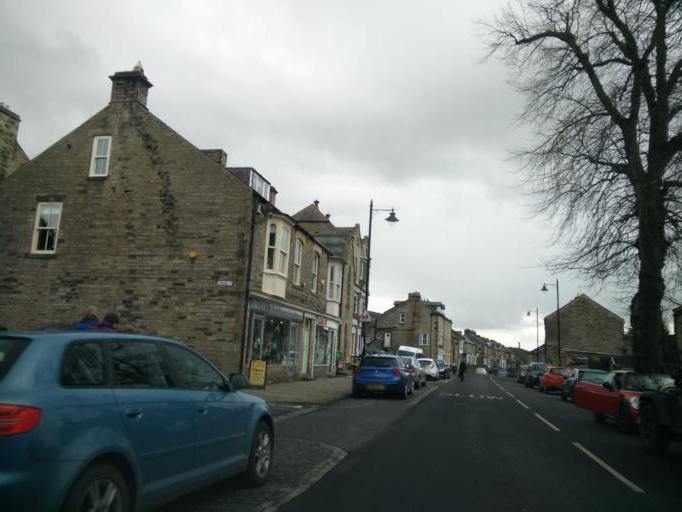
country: GB
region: England
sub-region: County Durham
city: Stanhope
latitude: 54.7466
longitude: -2.0047
